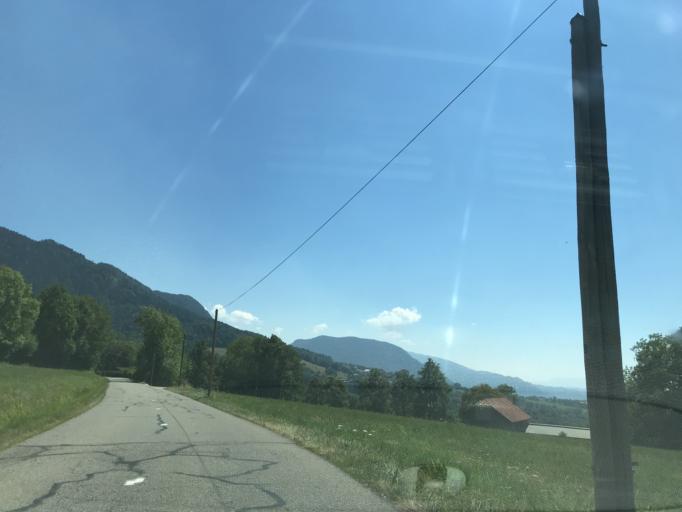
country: FR
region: Rhone-Alpes
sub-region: Departement de la Haute-Savoie
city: Thorens-Glieres
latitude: 45.9737
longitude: 6.2175
